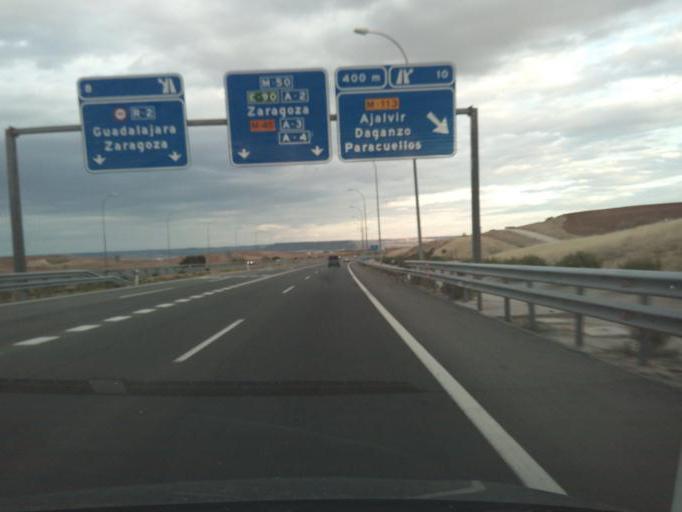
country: ES
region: Madrid
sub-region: Provincia de Madrid
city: Paracuellos de Jarama
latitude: 40.5240
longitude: -3.5103
